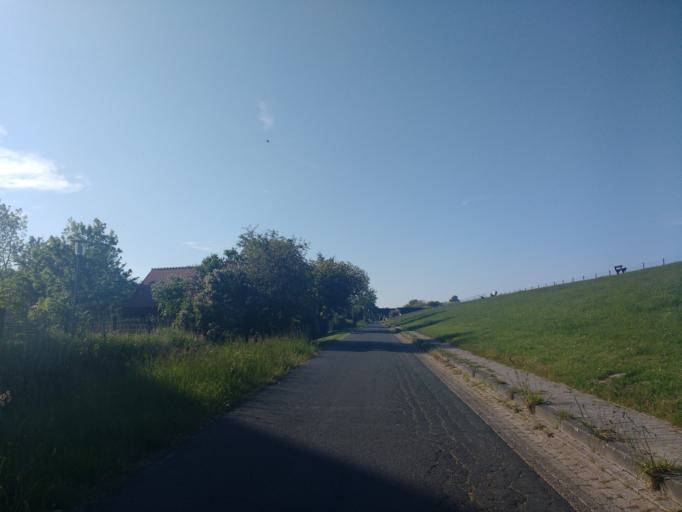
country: DE
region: Lower Saxony
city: Schillig
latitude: 53.6924
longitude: 8.0164
